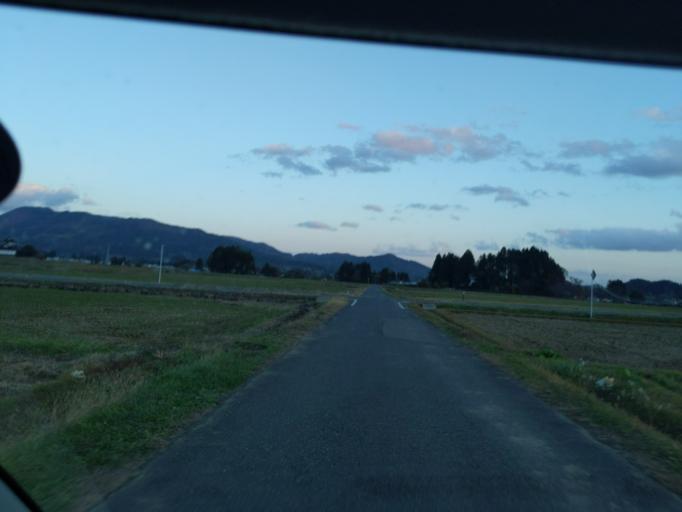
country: JP
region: Iwate
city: Ichinoseki
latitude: 39.0135
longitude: 141.0978
